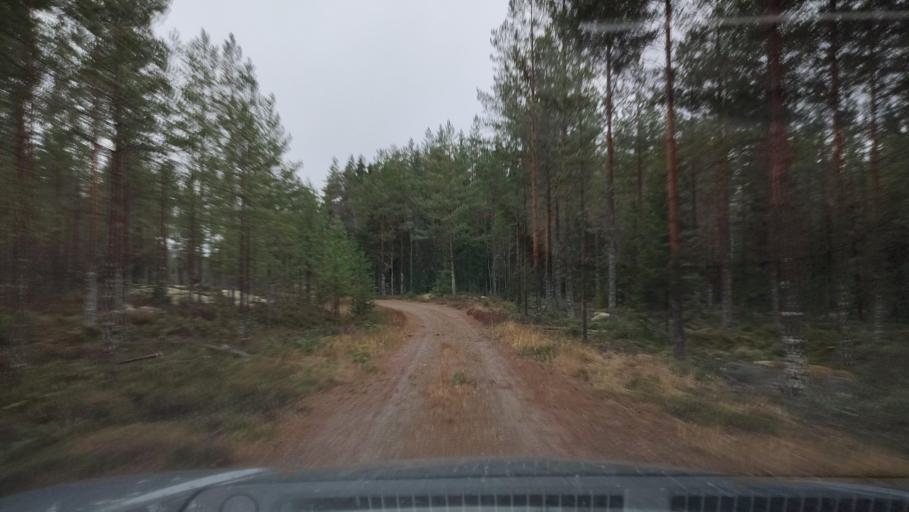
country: FI
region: Southern Ostrobothnia
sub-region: Suupohja
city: Karijoki
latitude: 62.1540
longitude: 21.5900
